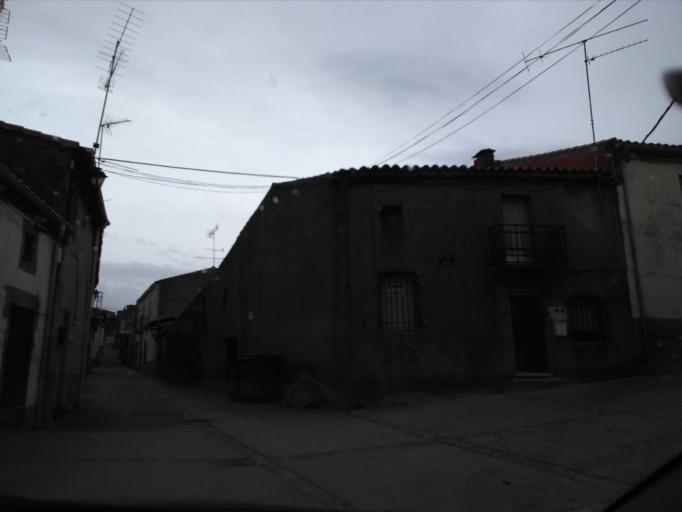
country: ES
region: Castille and Leon
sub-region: Provincia de Salamanca
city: San Felices de los Gallegos
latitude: 40.8486
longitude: -6.7093
